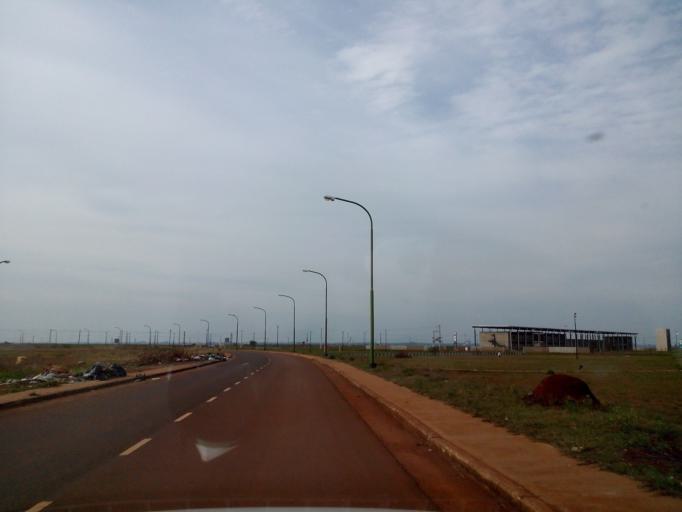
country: AR
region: Misiones
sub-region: Departamento de Capital
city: Posadas
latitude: -27.4194
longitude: -55.8881
